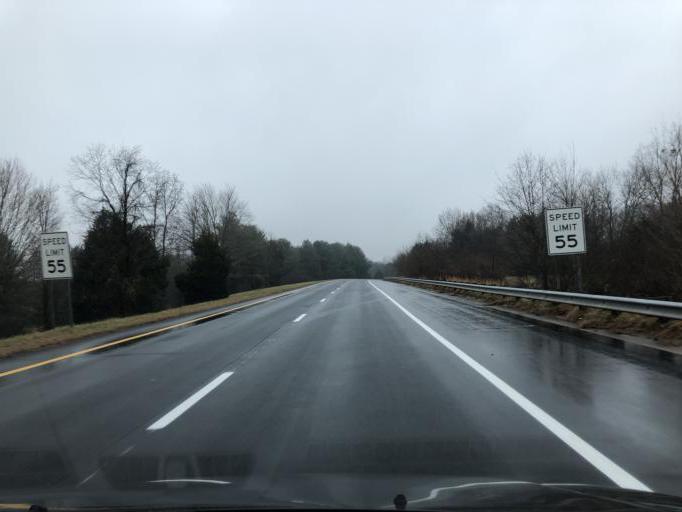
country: US
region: North Carolina
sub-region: Rutherford County
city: Forest City
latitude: 35.3136
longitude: -81.8722
